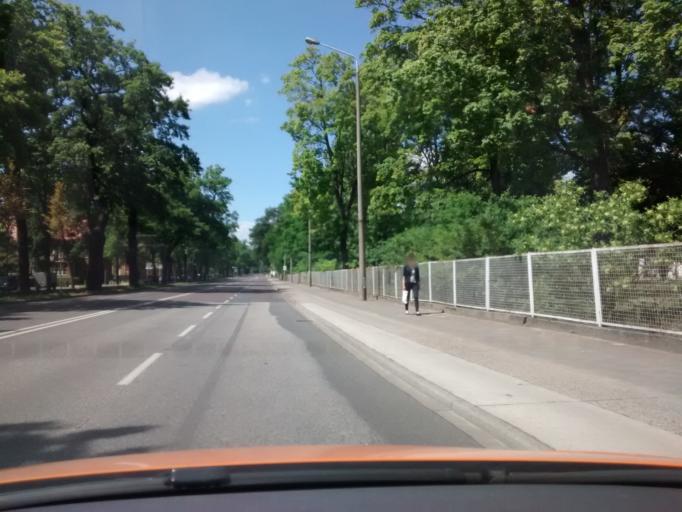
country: DE
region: Brandenburg
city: Potsdam
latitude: 52.3788
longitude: 13.0814
